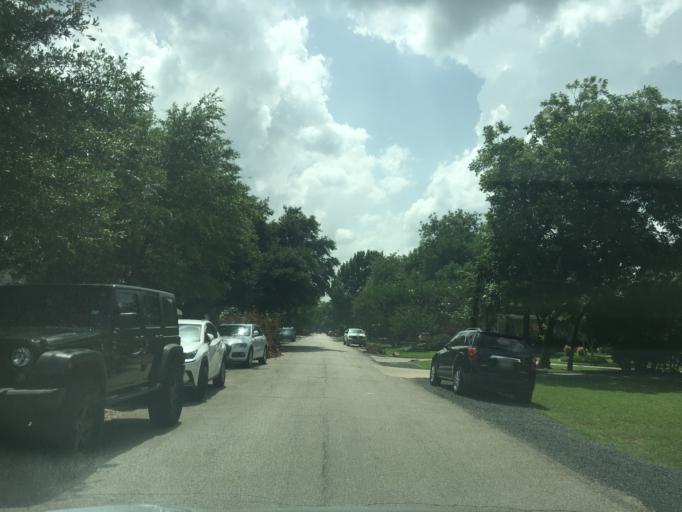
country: US
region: Texas
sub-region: Dallas County
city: University Park
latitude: 32.8885
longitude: -96.7986
